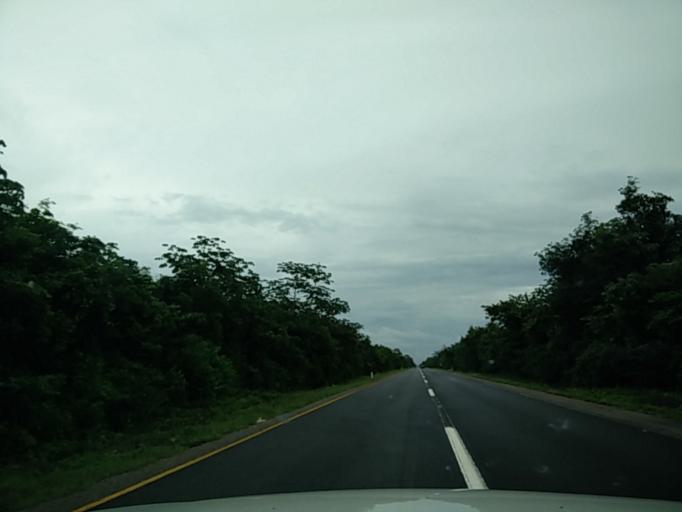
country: MX
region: Quintana Roo
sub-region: Lazaro Cardenas
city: Nuevo Xcan
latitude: 20.8828
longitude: -87.5785
